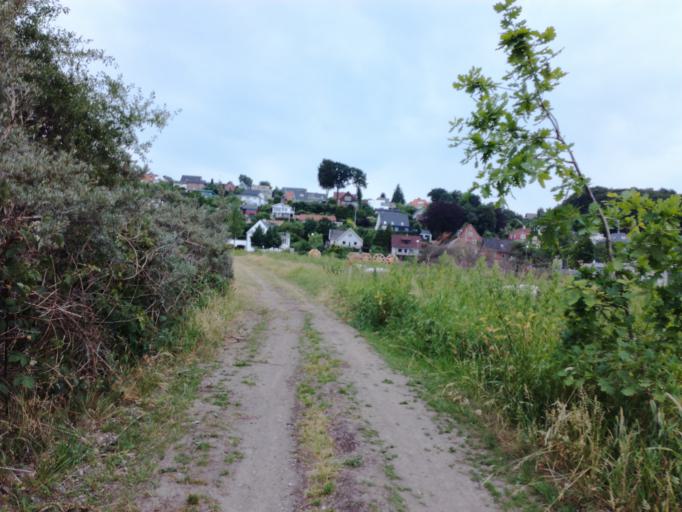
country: DK
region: South Denmark
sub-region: Vejle Kommune
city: Vejle
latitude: 55.7005
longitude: 9.5550
